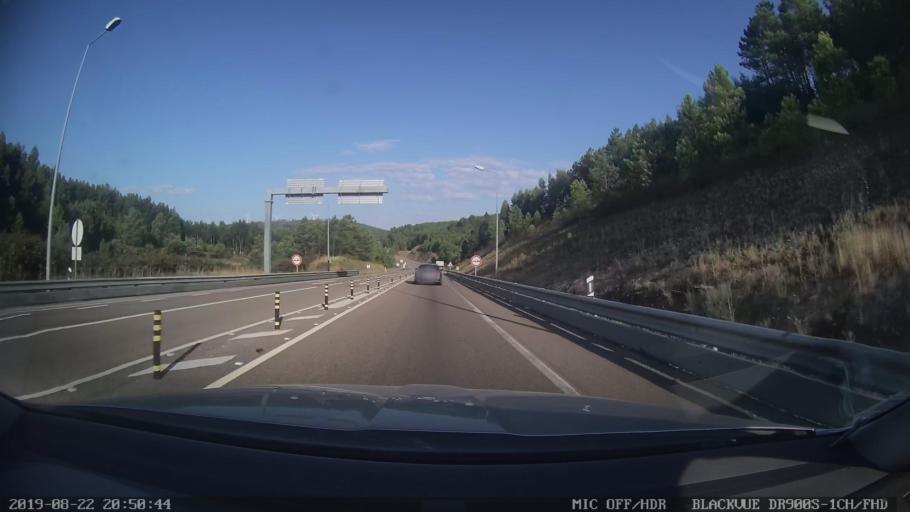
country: PT
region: Castelo Branco
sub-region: Proenca-A-Nova
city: Proenca-a-Nova
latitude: 39.7570
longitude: -7.9448
